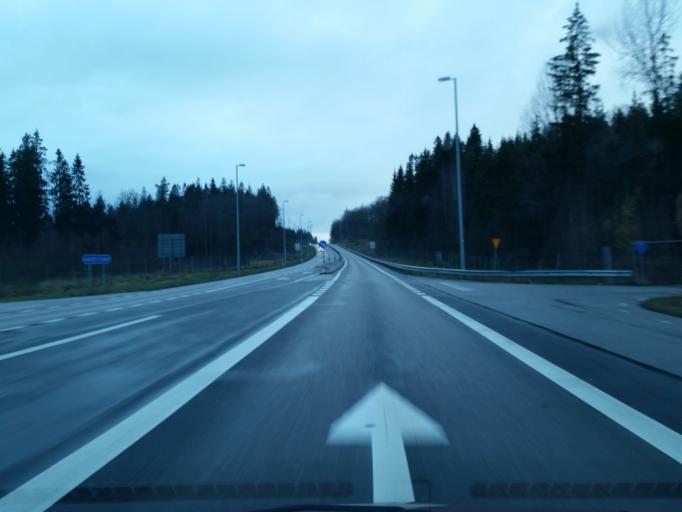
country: SE
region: Vaestra Goetaland
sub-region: Boras Kommun
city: Ganghester
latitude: 57.6745
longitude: 12.9933
